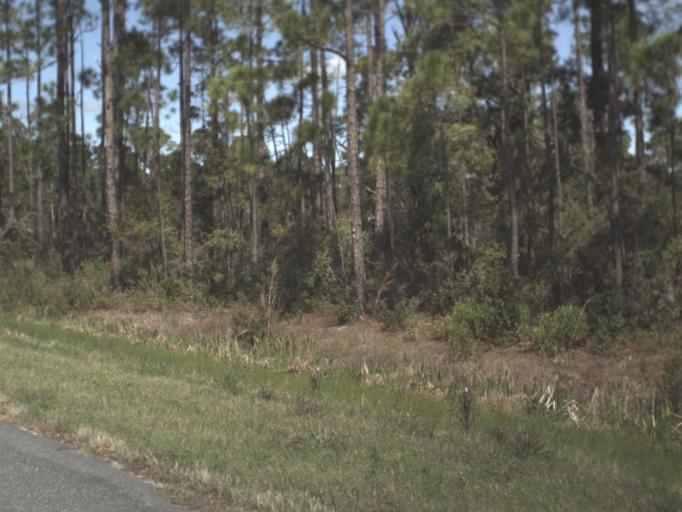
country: US
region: Florida
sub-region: Wakulla County
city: Crawfordville
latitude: 29.9912
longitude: -84.3932
